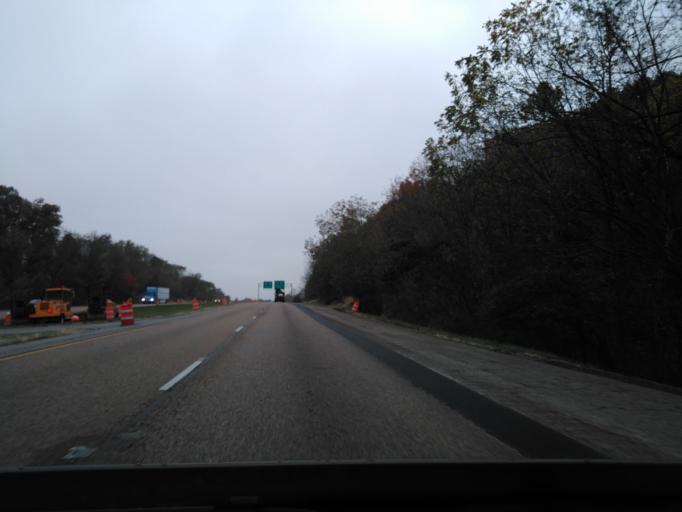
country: US
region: Illinois
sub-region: Madison County
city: Troy
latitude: 38.7548
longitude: -89.8847
